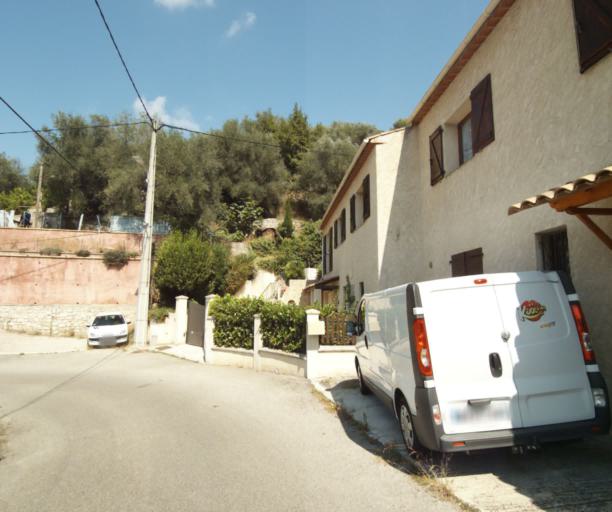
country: FR
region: Provence-Alpes-Cote d'Azur
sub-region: Departement des Alpes-Maritimes
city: Drap
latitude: 43.7602
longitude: 7.3251
